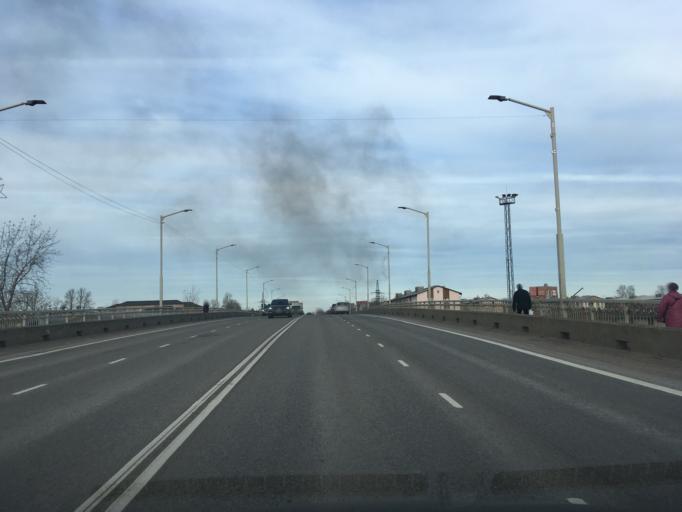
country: EE
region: Ida-Virumaa
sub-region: Narva linn
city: Narva
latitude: 59.3712
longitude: 28.1842
